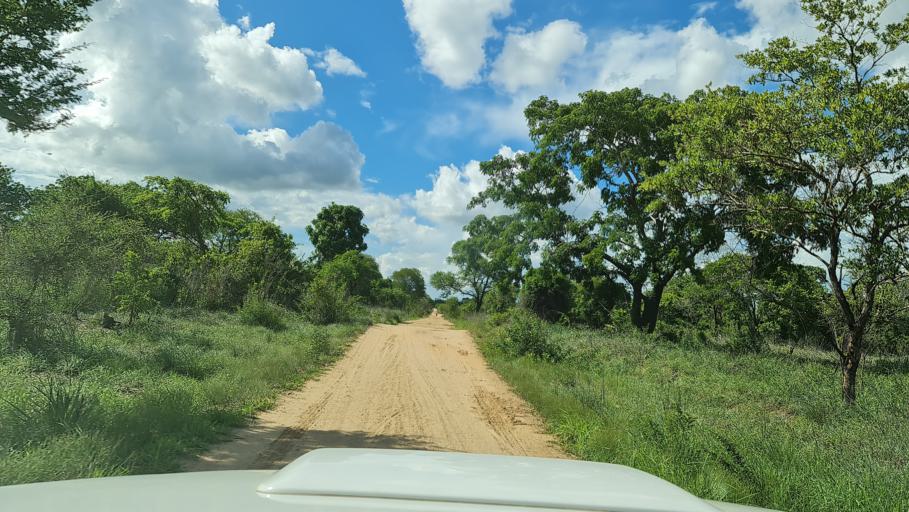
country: MZ
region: Nampula
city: Ilha de Mocambique
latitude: -15.4014
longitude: 40.2369
